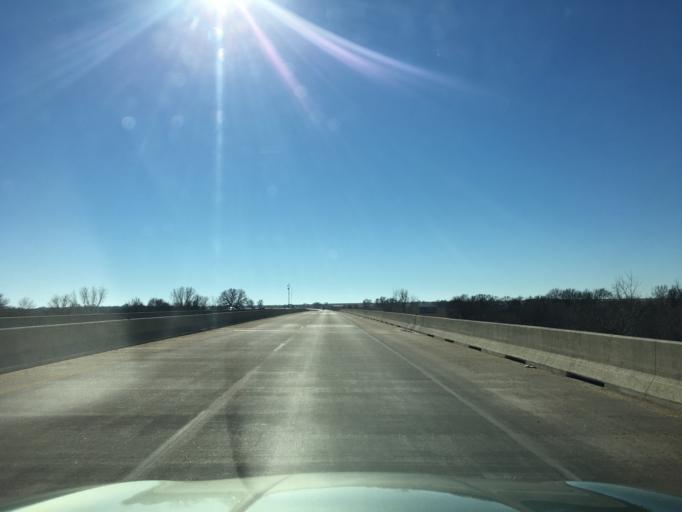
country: US
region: Oklahoma
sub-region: Kay County
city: Blackwell
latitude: 36.9087
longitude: -97.3529
